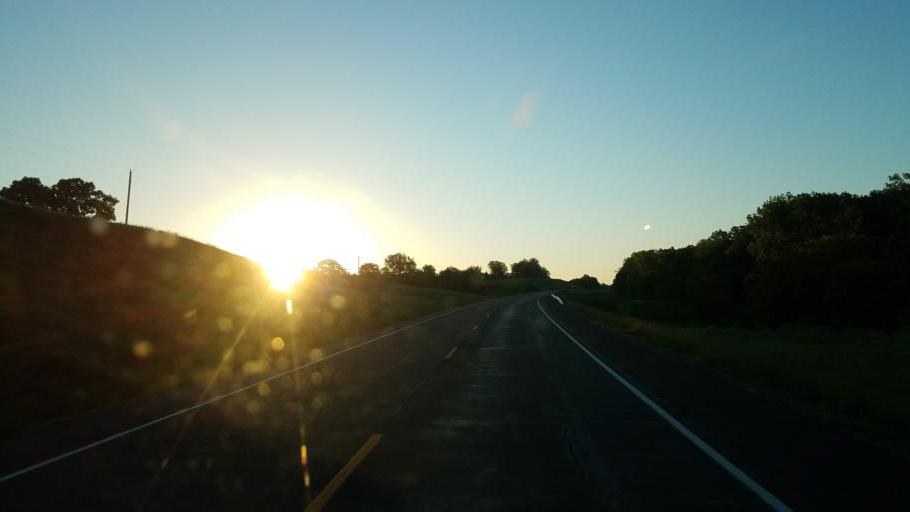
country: US
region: Missouri
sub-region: Schuyler County
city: Lancaster
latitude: 40.4885
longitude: -92.6506
